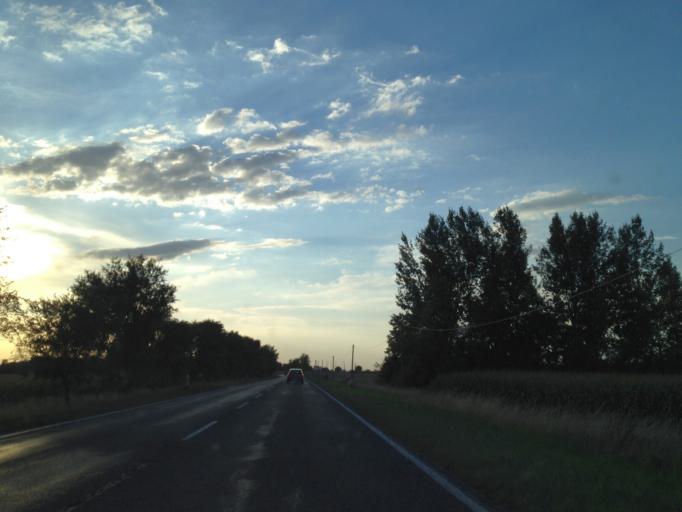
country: HU
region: Gyor-Moson-Sopron
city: Mosonszentmiklos
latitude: 47.7606
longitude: 17.4396
